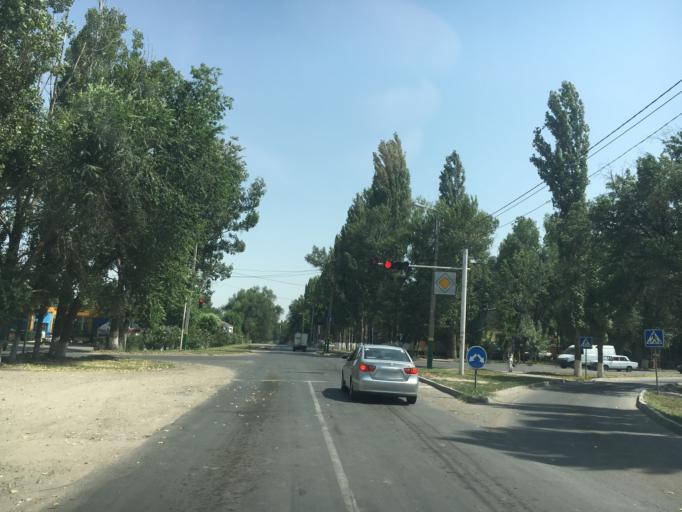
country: KZ
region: Zhambyl
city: Taraz
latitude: 42.8884
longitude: 71.3441
